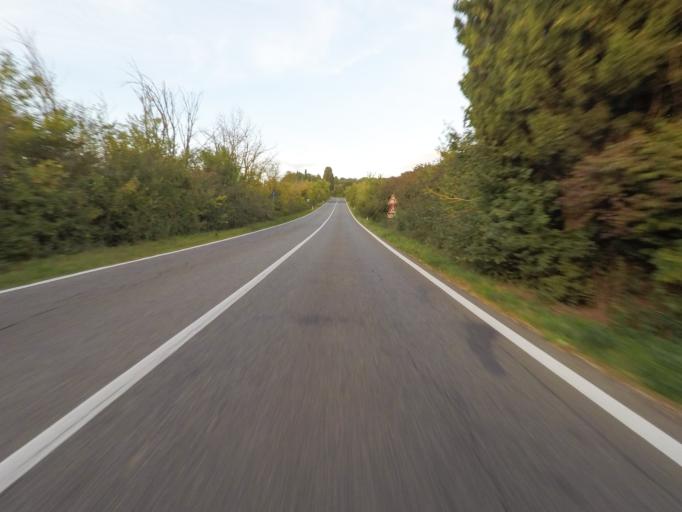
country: IT
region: Tuscany
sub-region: Provincia di Siena
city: Pienza
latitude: 43.0981
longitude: 11.6946
